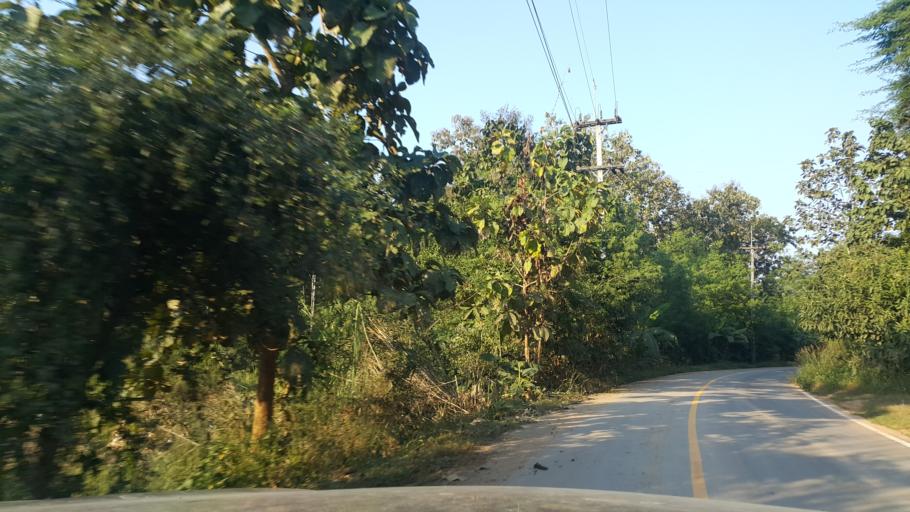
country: TH
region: Lampang
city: Hang Chat
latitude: 18.3421
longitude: 99.2506
